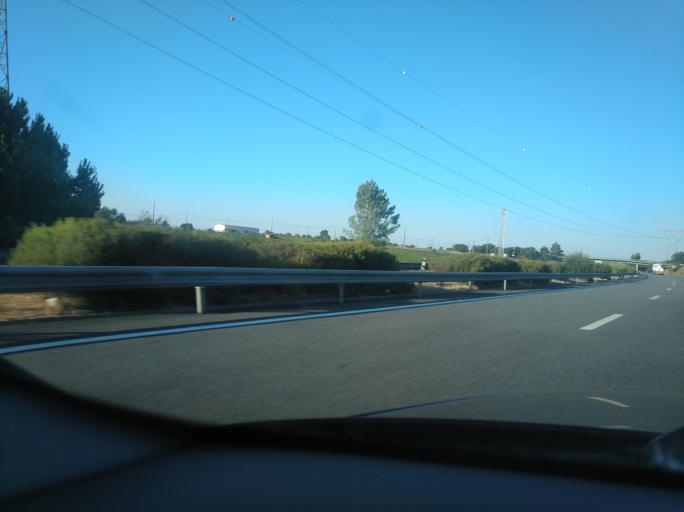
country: PT
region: Setubal
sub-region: Palmela
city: Palmela
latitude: 38.5864
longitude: -8.7716
